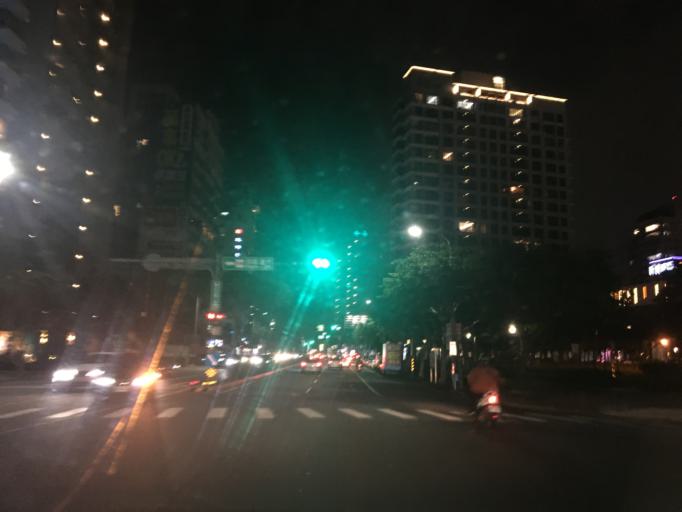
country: TW
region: Taiwan
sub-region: Taoyuan
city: Taoyuan
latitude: 25.0737
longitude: 121.3668
